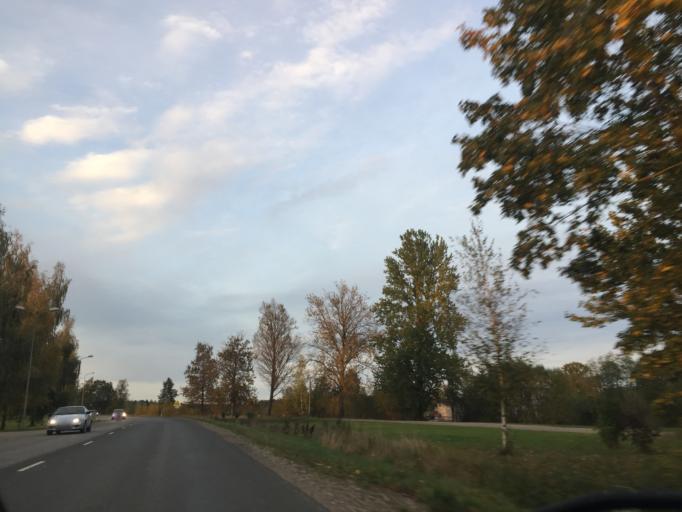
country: LV
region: Dobeles Rajons
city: Dobele
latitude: 56.7406
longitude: 23.3931
